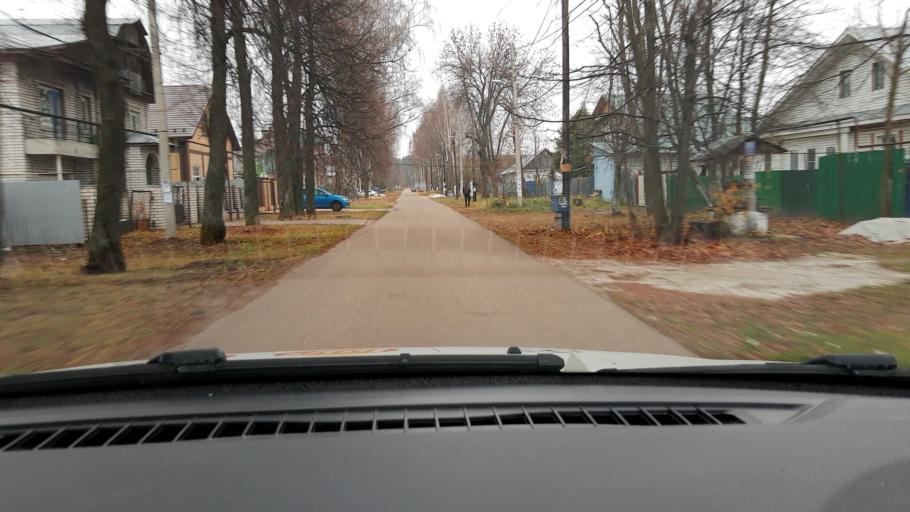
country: RU
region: Nizjnij Novgorod
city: Gorbatovka
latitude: 56.2025
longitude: 43.7695
